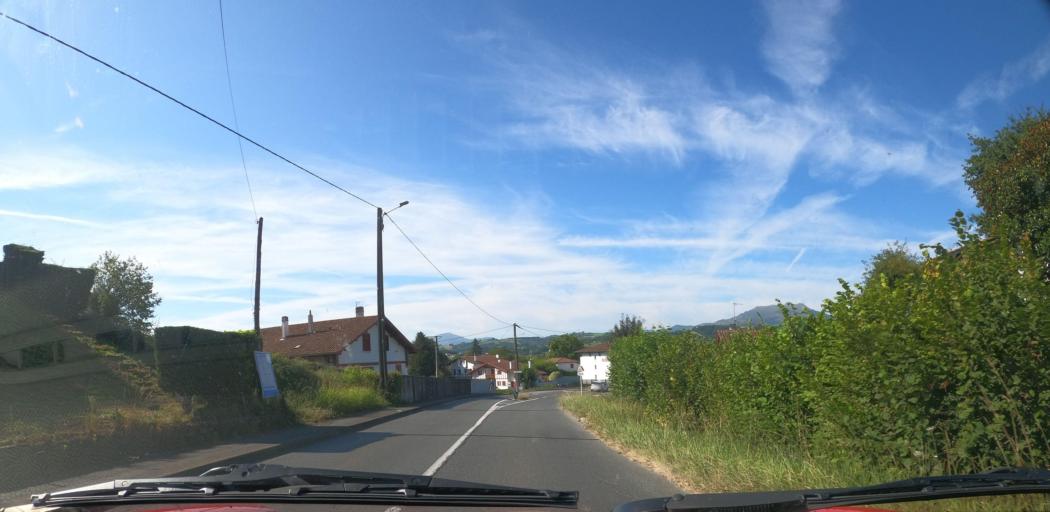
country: FR
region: Aquitaine
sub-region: Departement des Pyrenees-Atlantiques
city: Saint-Pee-sur-Nivelle
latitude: 43.3591
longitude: -1.5475
